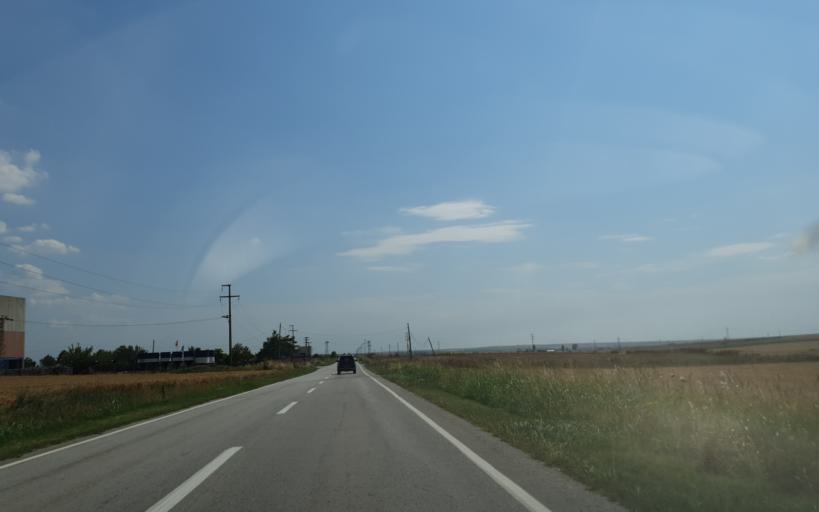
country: TR
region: Kirklareli
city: Buyukkaristiran
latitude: 41.3192
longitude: 27.5226
